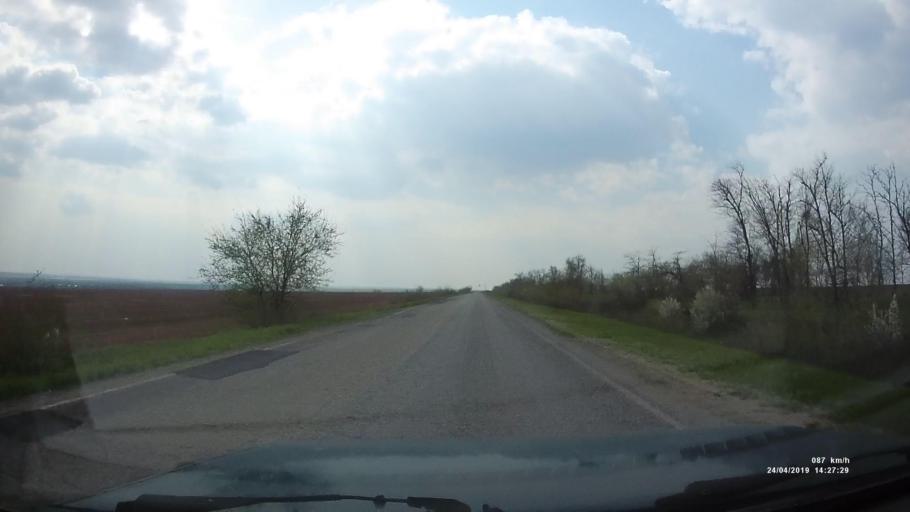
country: RU
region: Kalmykiya
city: Arshan'
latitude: 46.3338
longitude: 44.0424
